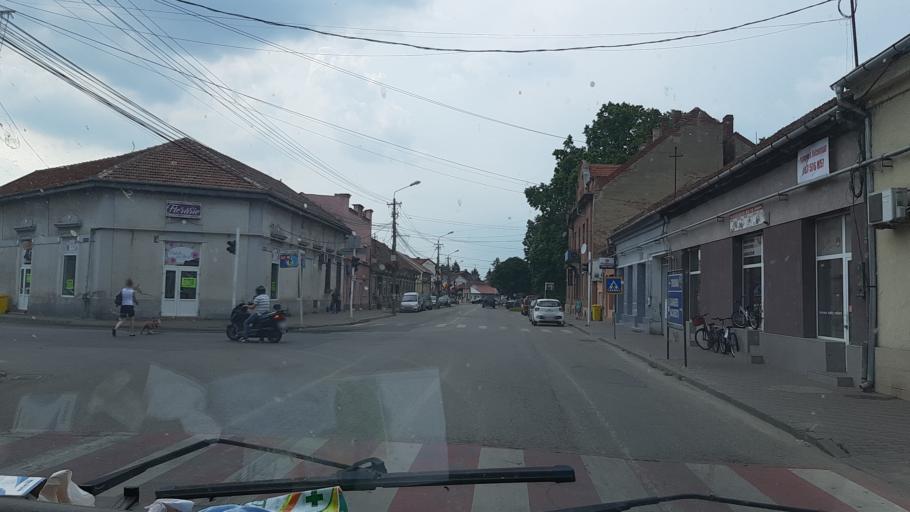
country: RO
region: Timis
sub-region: Municipiul Lugoj
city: Lugoj
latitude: 45.6859
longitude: 21.8991
